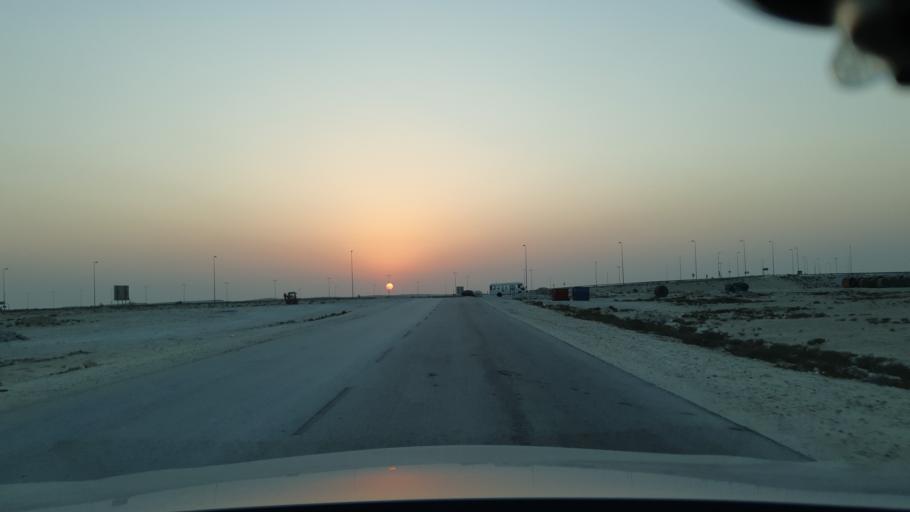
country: BH
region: Central Governorate
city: Dar Kulayb
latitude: 25.9558
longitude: 50.5984
